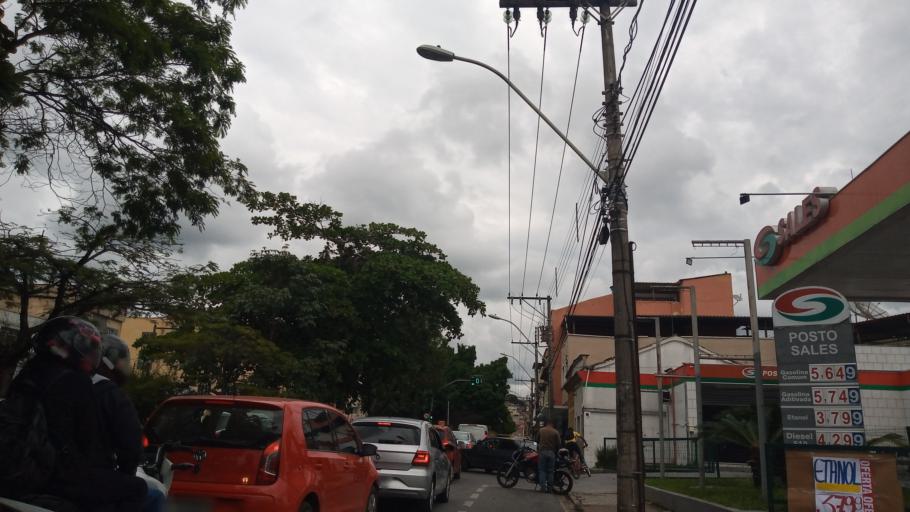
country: BR
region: Minas Gerais
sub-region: Sao Joao Del Rei
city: Sao Joao del Rei
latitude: -21.1276
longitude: -44.2497
